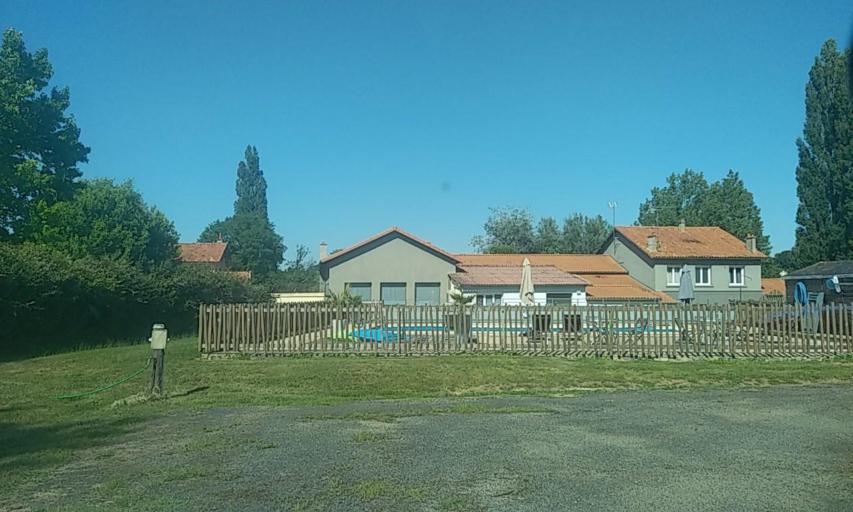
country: FR
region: Poitou-Charentes
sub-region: Departement des Deux-Sevres
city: Moncoutant
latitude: 46.7128
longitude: -0.6082
